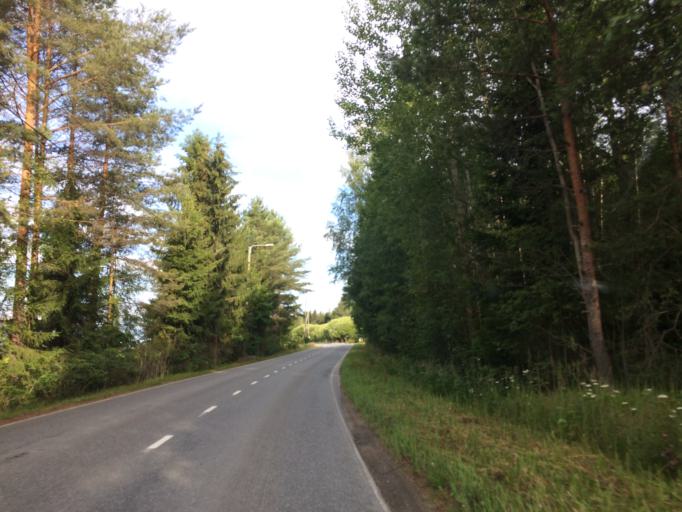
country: FI
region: Haeme
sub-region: Haemeenlinna
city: Janakkala
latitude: 60.9292
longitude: 24.5752
